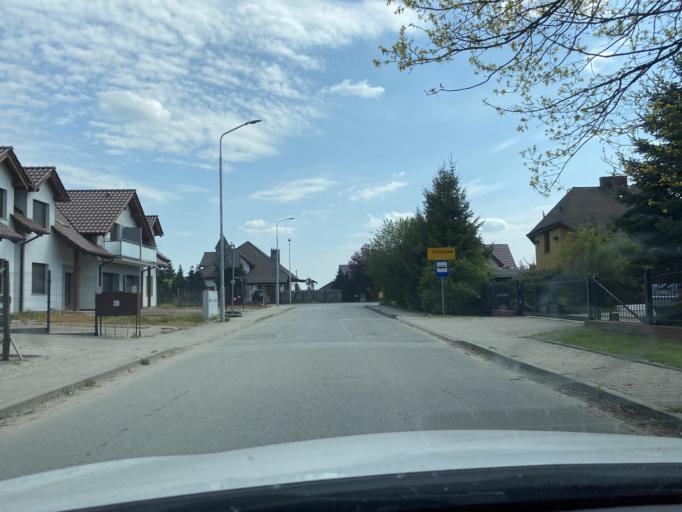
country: PL
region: Lower Silesian Voivodeship
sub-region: Powiat wroclawski
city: Mirkow
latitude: 51.1601
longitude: 17.1732
